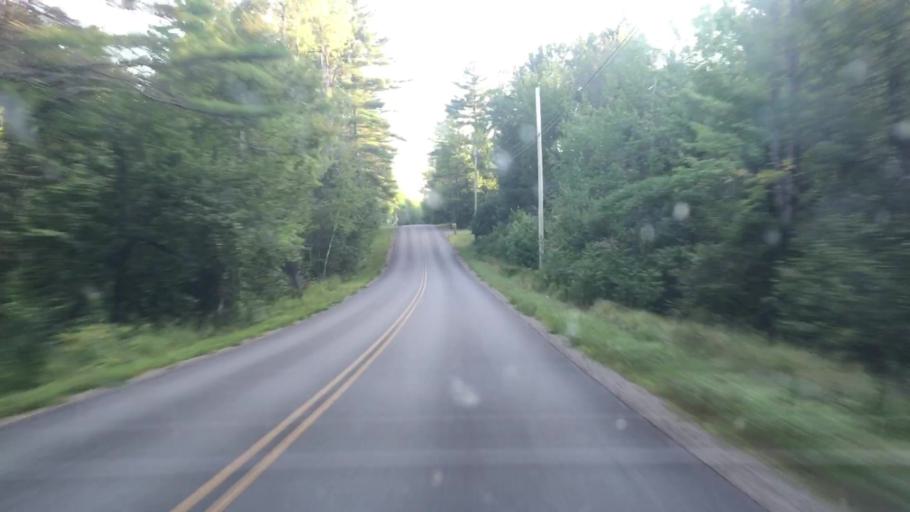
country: US
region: Maine
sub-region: Penobscot County
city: Hampden
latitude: 44.7011
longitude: -68.8933
